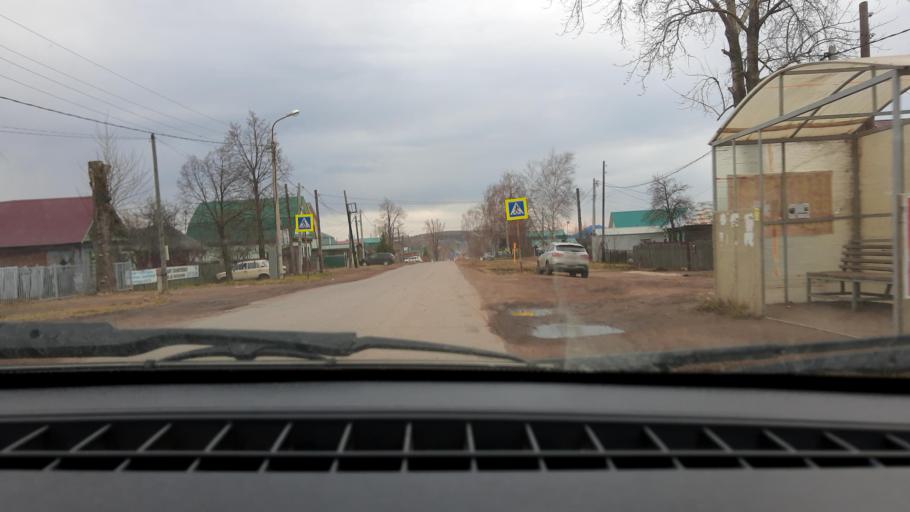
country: RU
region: Bashkortostan
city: Ufa
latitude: 54.8468
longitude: 56.1530
